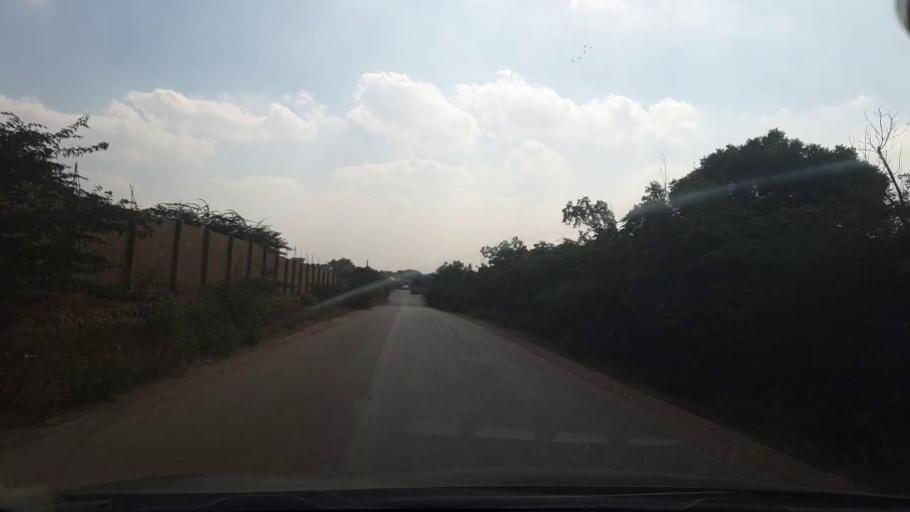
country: PK
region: Sindh
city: Malir Cantonment
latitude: 25.0095
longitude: 67.3552
